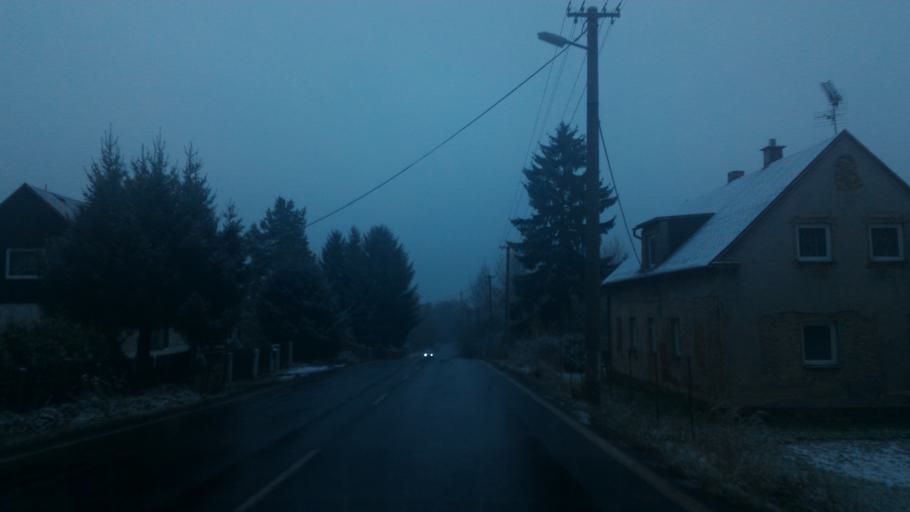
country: CZ
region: Ustecky
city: Jirikov
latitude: 50.9753
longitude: 14.5655
